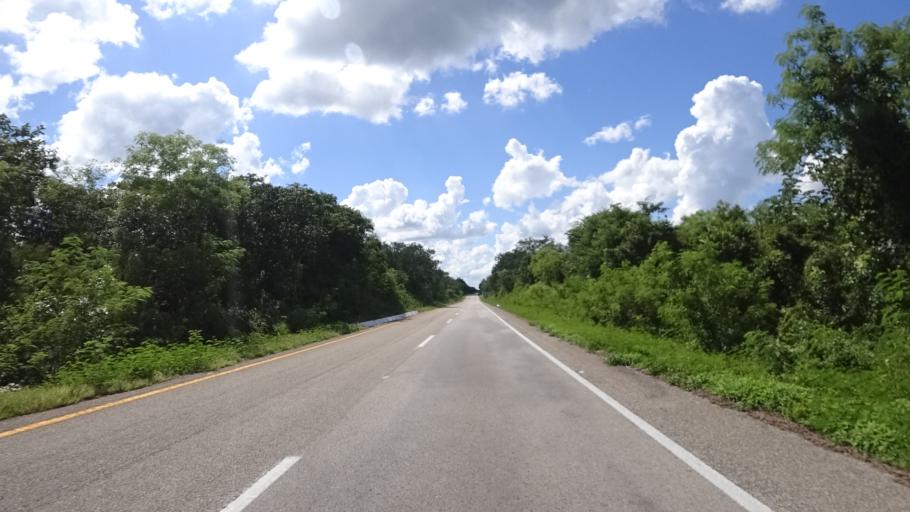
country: MX
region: Yucatan
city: Chichen-Itza
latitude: 20.7172
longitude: -88.5203
